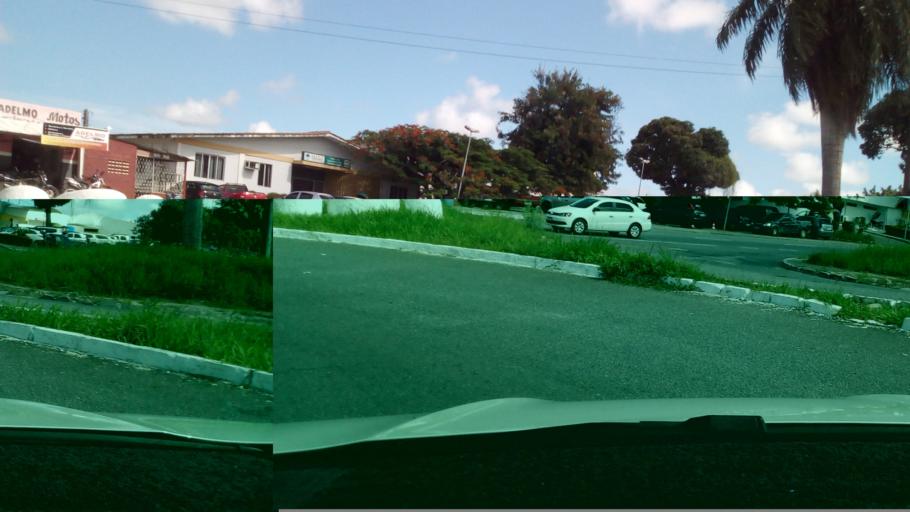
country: BR
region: Paraiba
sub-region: Joao Pessoa
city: Joao Pessoa
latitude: -7.1451
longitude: -34.8918
